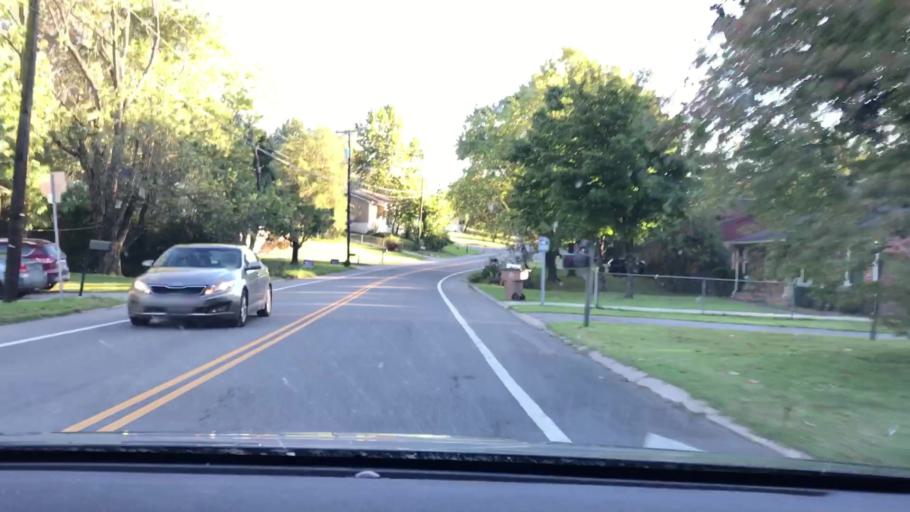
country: US
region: Tennessee
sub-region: Williamson County
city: Brentwood Estates
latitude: 36.0512
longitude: -86.7028
